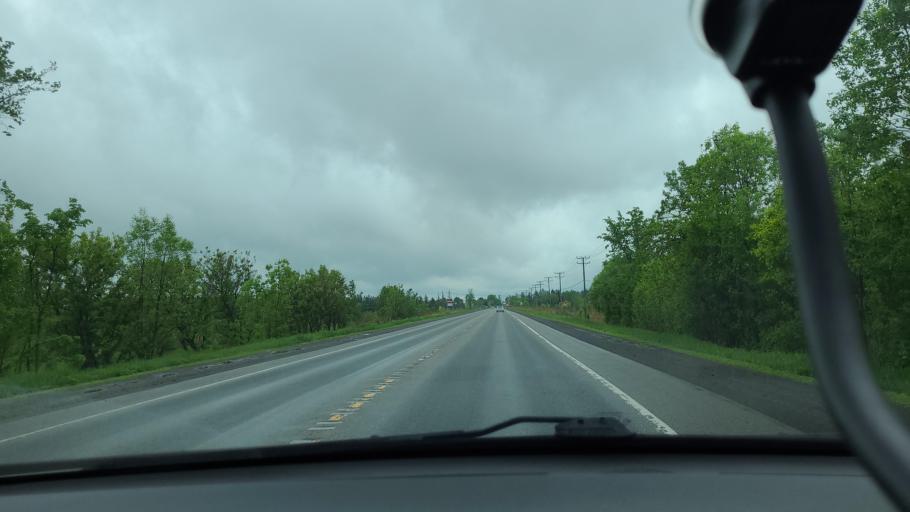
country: CA
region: Quebec
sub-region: Laurentides
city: Saint-Jerome
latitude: 45.7390
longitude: -74.0357
